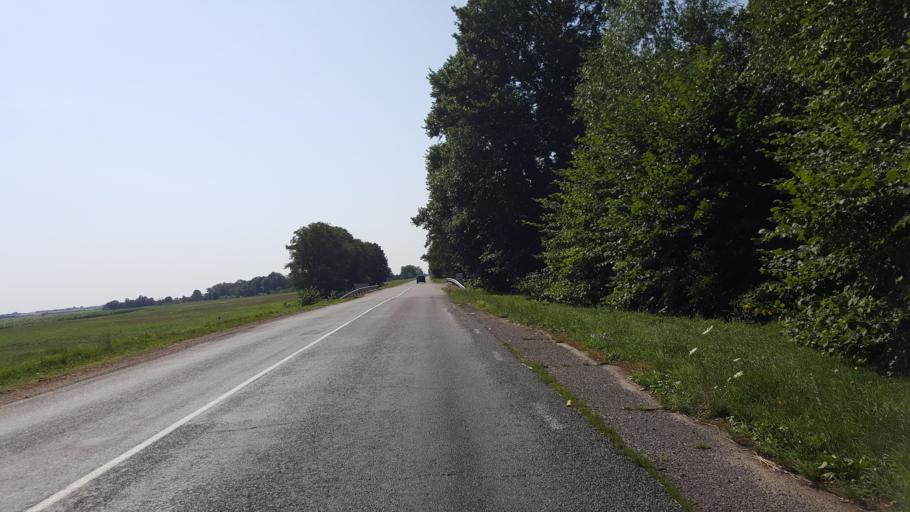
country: BY
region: Brest
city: Zhabinka
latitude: 52.2354
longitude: 23.9809
